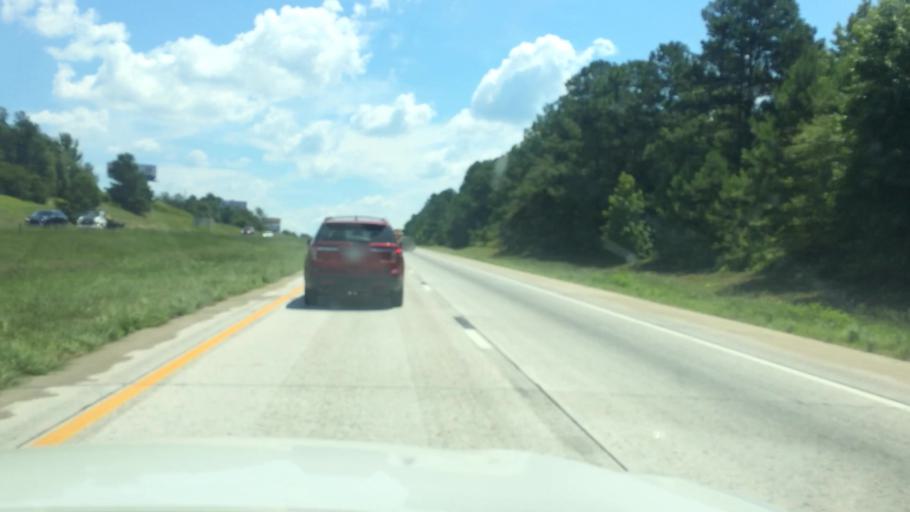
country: US
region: South Carolina
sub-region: Aiken County
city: Belvedere
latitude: 33.5463
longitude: -81.9662
